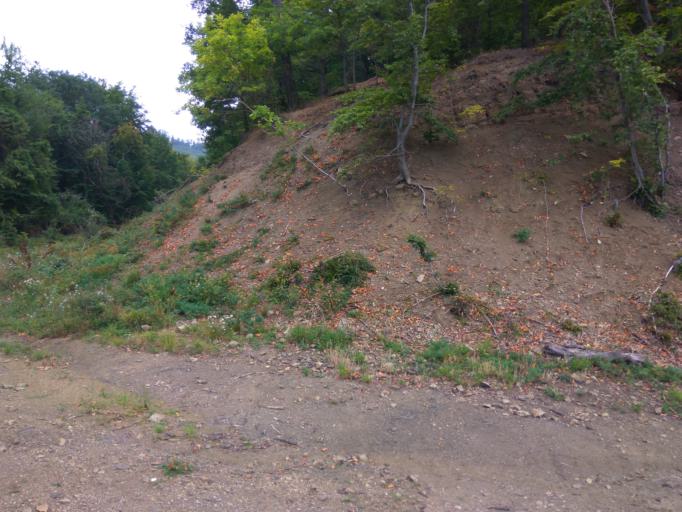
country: HU
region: Heves
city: Paradsasvar
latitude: 47.9124
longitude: 19.9622
